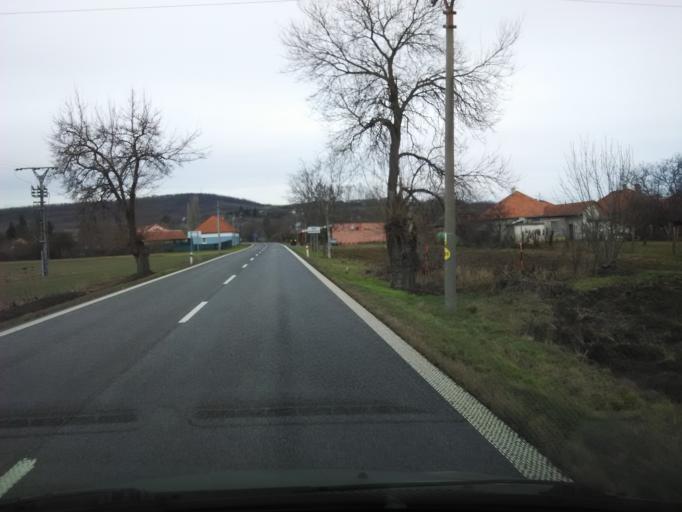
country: SK
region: Nitriansky
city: Tlmace
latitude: 48.2706
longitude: 18.5115
